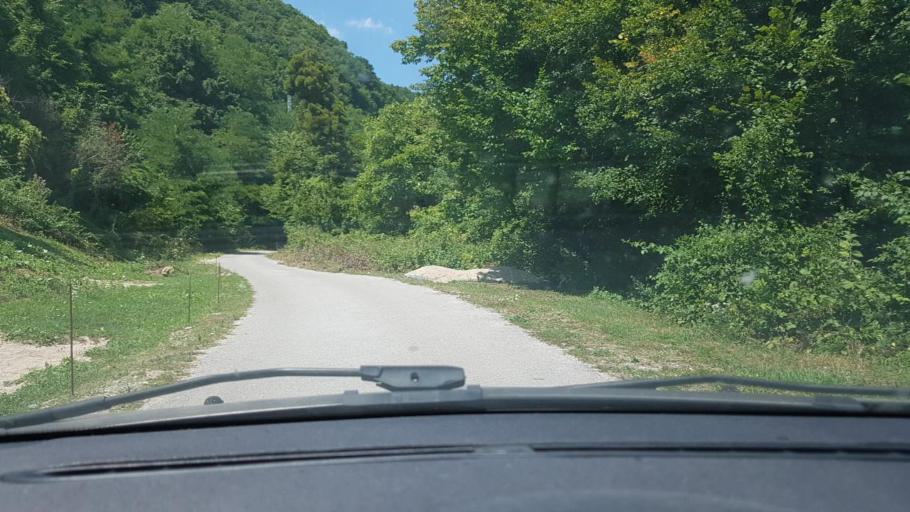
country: BA
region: Federation of Bosnia and Herzegovina
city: Orasac
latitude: 44.5612
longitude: 16.0840
